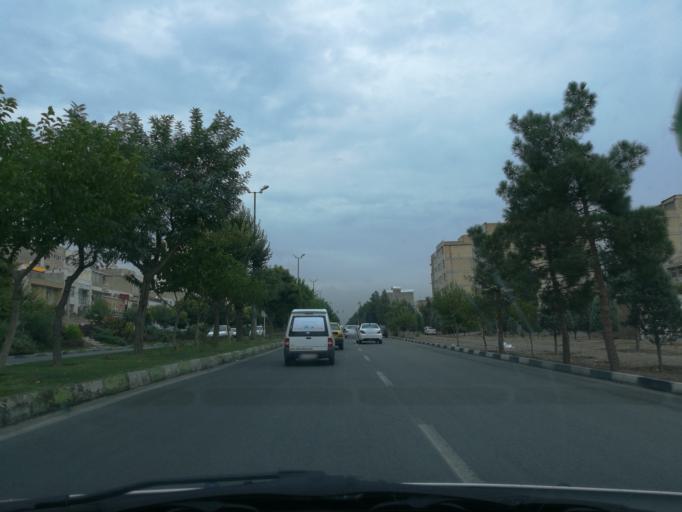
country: IR
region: Alborz
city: Karaj
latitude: 35.8608
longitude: 50.9398
